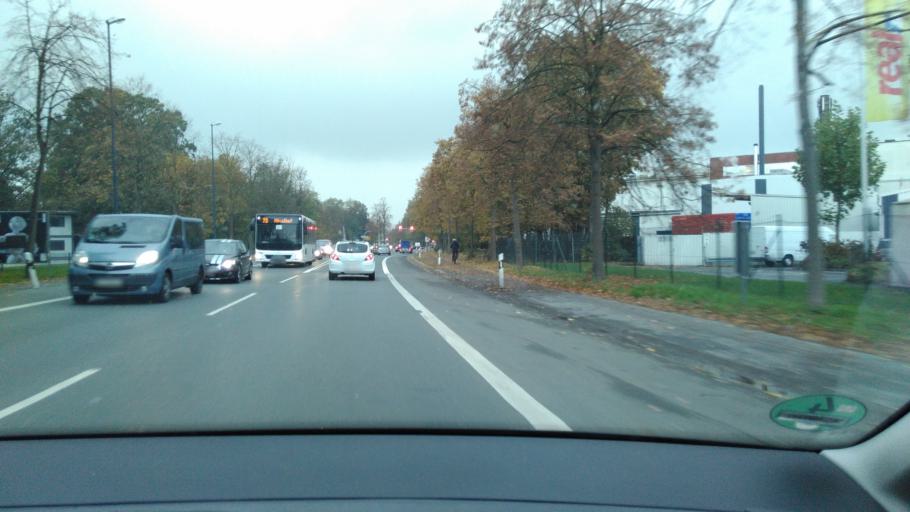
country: DE
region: North Rhine-Westphalia
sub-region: Regierungsbezirk Detmold
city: Guetersloh
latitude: 51.8991
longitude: 8.4005
